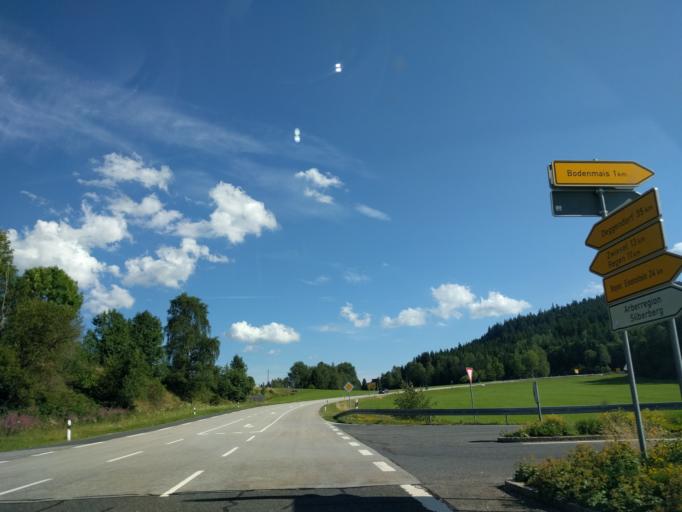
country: DE
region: Bavaria
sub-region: Lower Bavaria
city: Bodenmais
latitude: 49.0544
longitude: 13.1089
